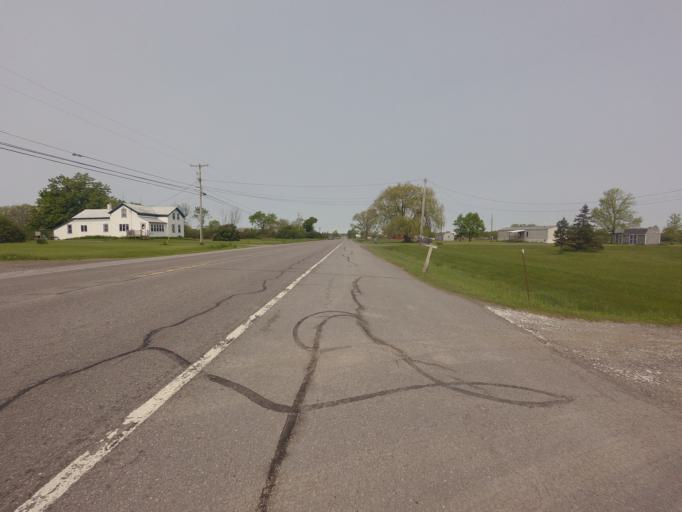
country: US
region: New York
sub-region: Jefferson County
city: Dexter
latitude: 44.0423
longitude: -76.0817
